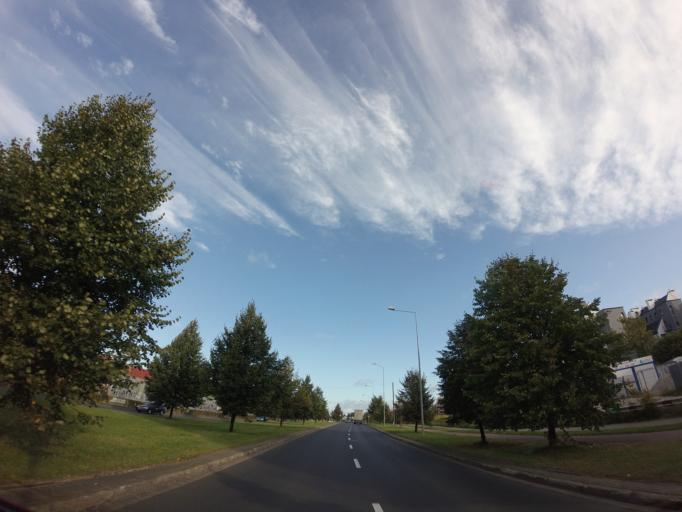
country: PL
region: West Pomeranian Voivodeship
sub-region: Szczecin
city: Szczecin
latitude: 53.4391
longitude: 14.4889
